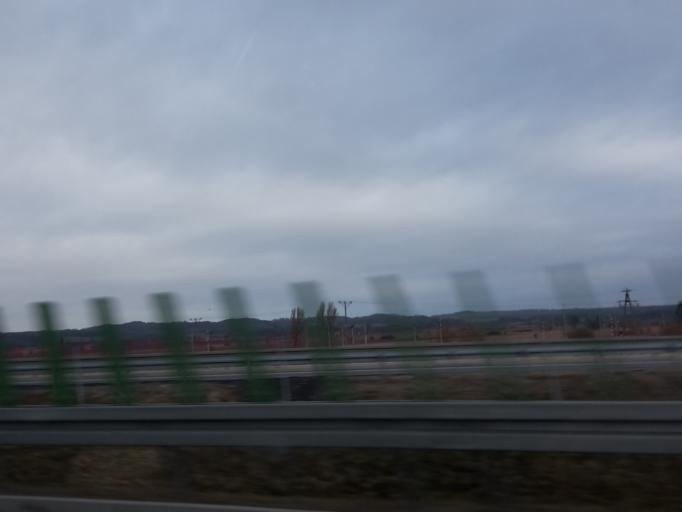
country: PL
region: Warmian-Masurian Voivodeship
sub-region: Powiat elblaski
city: Paslek
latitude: 54.0968
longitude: 19.5623
